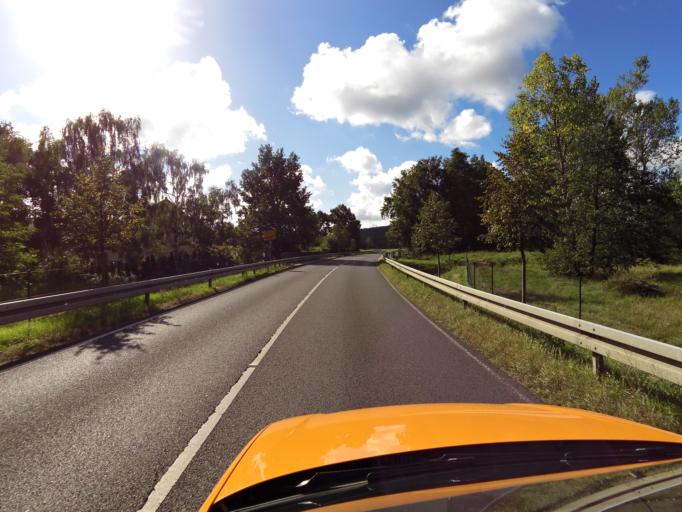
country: DE
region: Brandenburg
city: Michendorf
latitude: 52.3220
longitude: 13.1193
